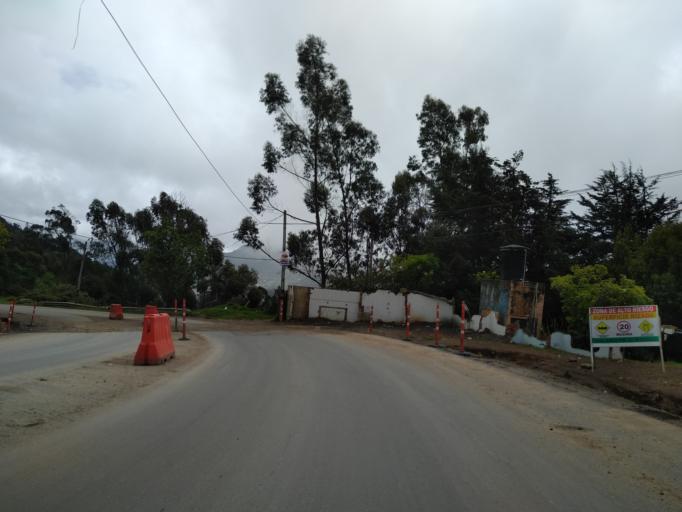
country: CO
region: Bogota D.C.
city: Barrio San Luis
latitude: 4.6602
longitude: -74.0054
